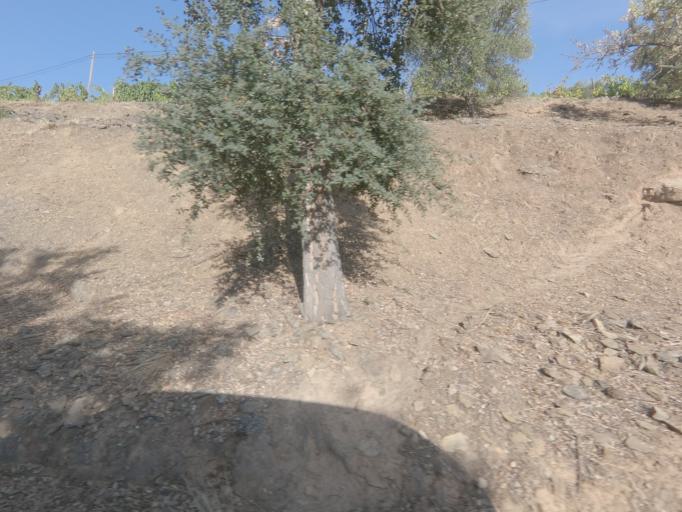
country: PT
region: Vila Real
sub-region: Sabrosa
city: Vilela
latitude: 41.2109
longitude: -7.5405
